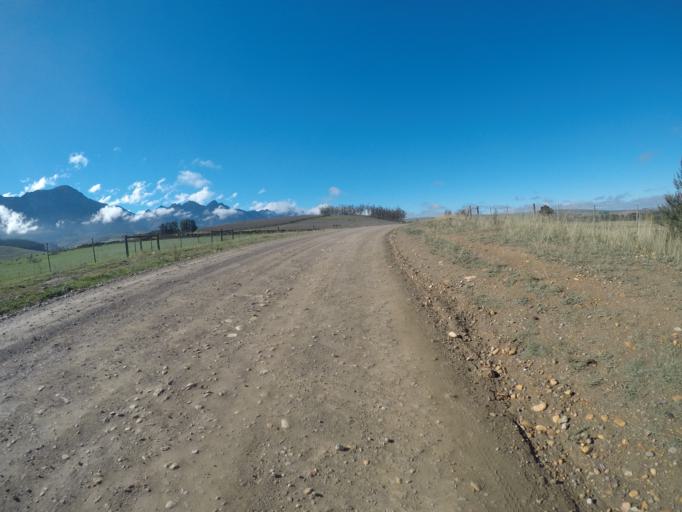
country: ZA
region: Western Cape
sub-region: Overberg District Municipality
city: Caledon
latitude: -34.0954
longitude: 19.6840
